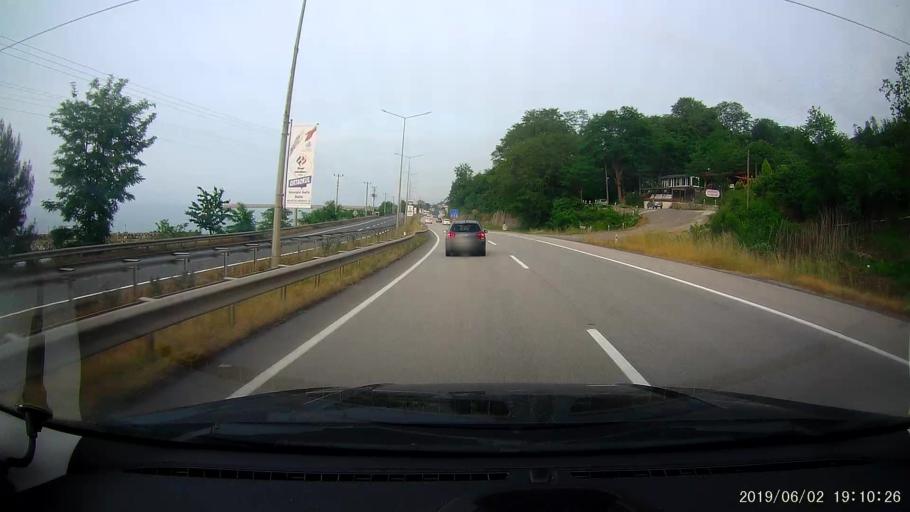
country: TR
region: Ordu
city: Gulyali
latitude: 40.9688
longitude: 38.0445
